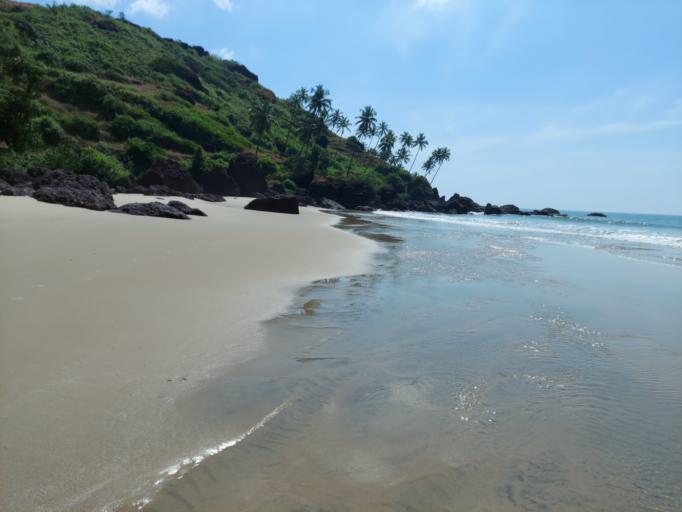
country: IN
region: Maharashtra
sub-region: Sindhudurg
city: Vengurla
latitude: 15.9184
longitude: 73.5673
